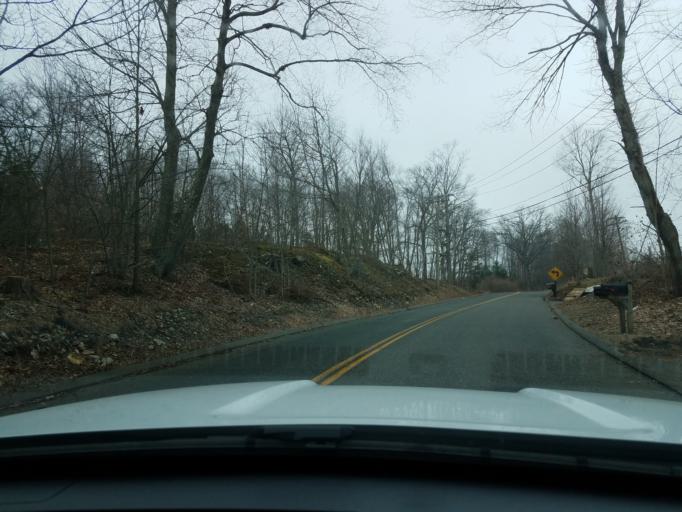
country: US
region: Connecticut
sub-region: New Haven County
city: Naugatuck
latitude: 41.4360
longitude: -73.0296
